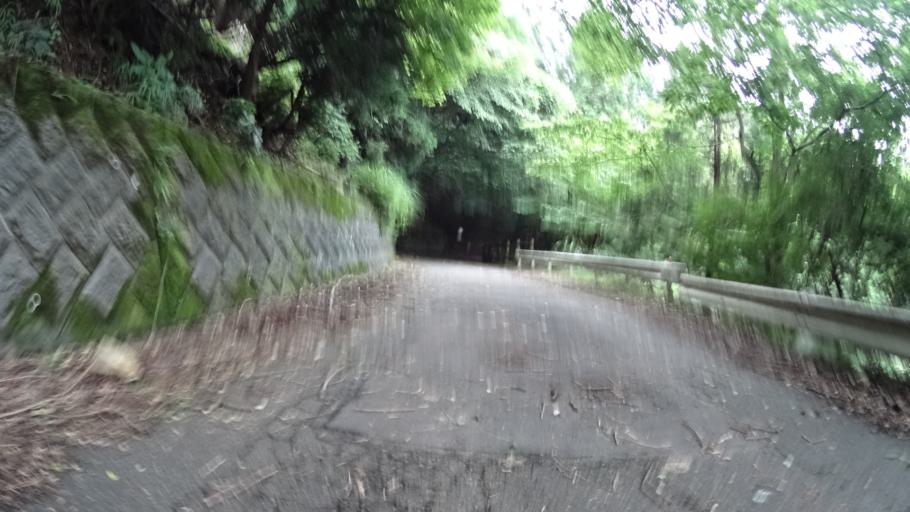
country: JP
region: Kanagawa
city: Atsugi
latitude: 35.5014
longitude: 139.2747
